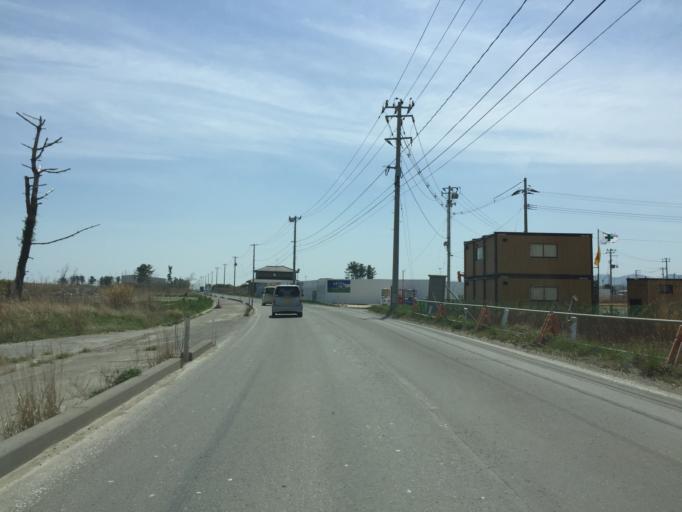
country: JP
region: Miyagi
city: Watari
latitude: 37.9686
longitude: 140.9070
